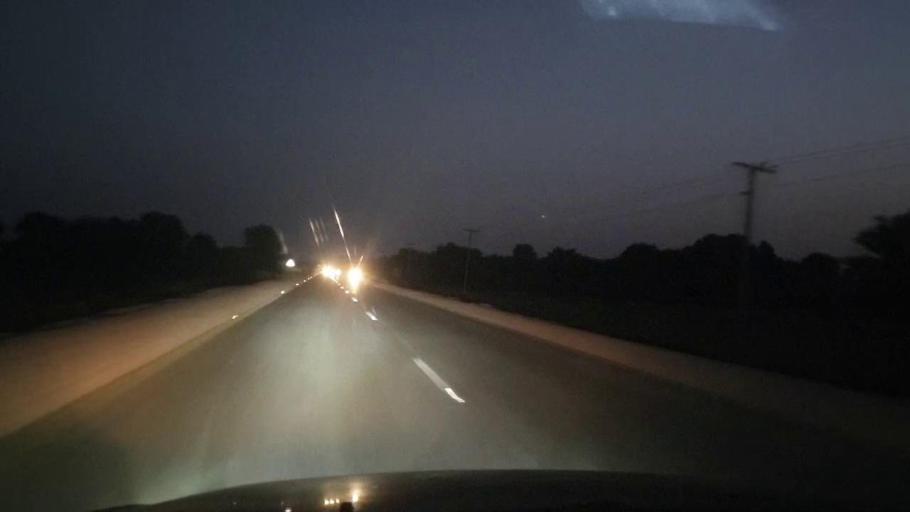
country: PK
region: Sindh
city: Chambar
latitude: 25.3248
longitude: 68.8007
